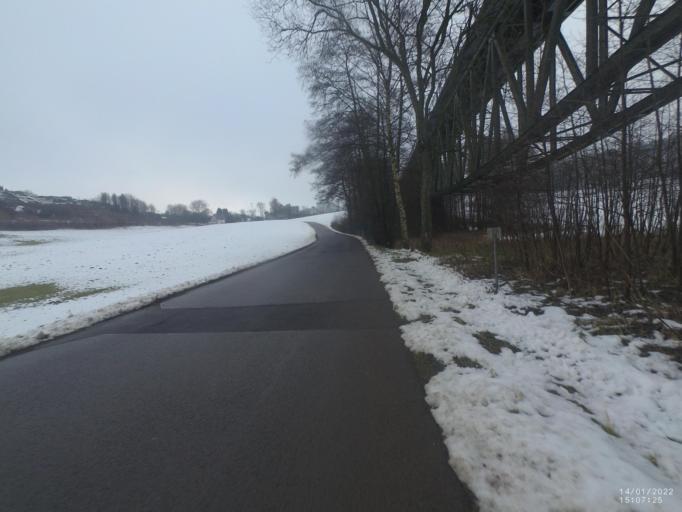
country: DE
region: North Rhine-Westphalia
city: Meinerzhagen
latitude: 51.1025
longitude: 7.6625
